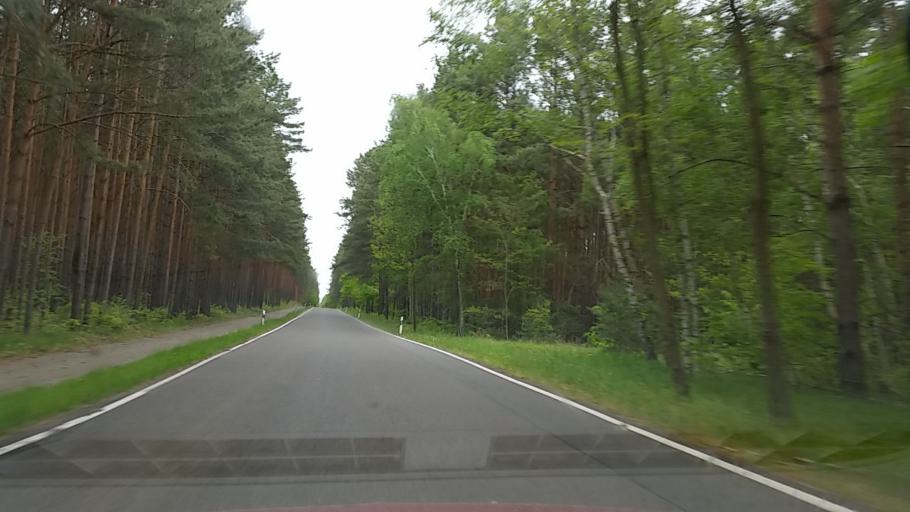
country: DE
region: Brandenburg
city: Reichenwalde
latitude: 52.2984
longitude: 13.9846
